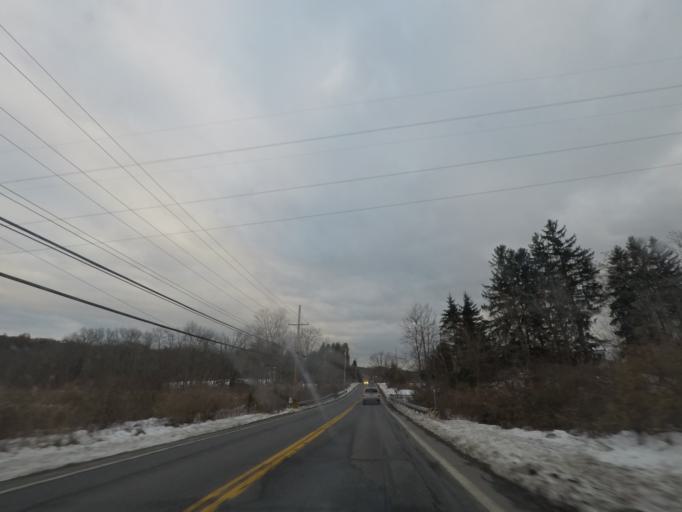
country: US
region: New York
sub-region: Ulster County
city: Plattekill
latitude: 41.5790
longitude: -74.0668
